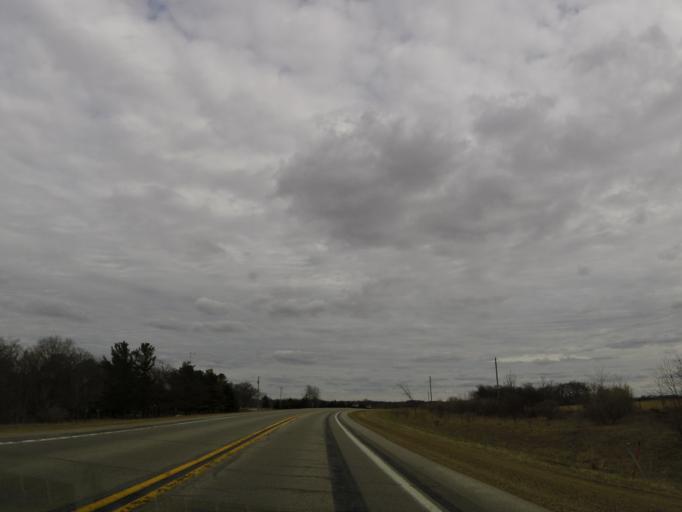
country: US
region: Minnesota
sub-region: Fillmore County
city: Spring Valley
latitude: 43.4720
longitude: -92.3235
